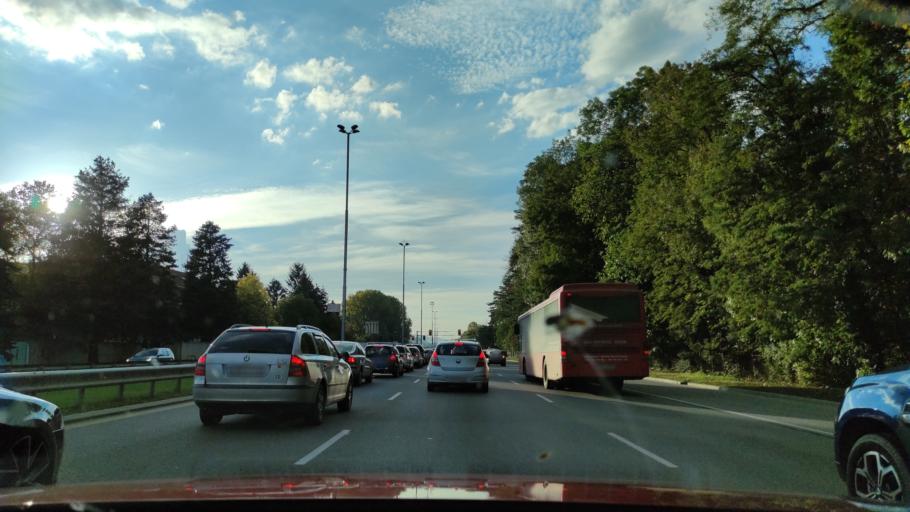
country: BG
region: Sofia-Capital
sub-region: Stolichna Obshtina
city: Sofia
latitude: 42.6357
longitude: 23.4298
